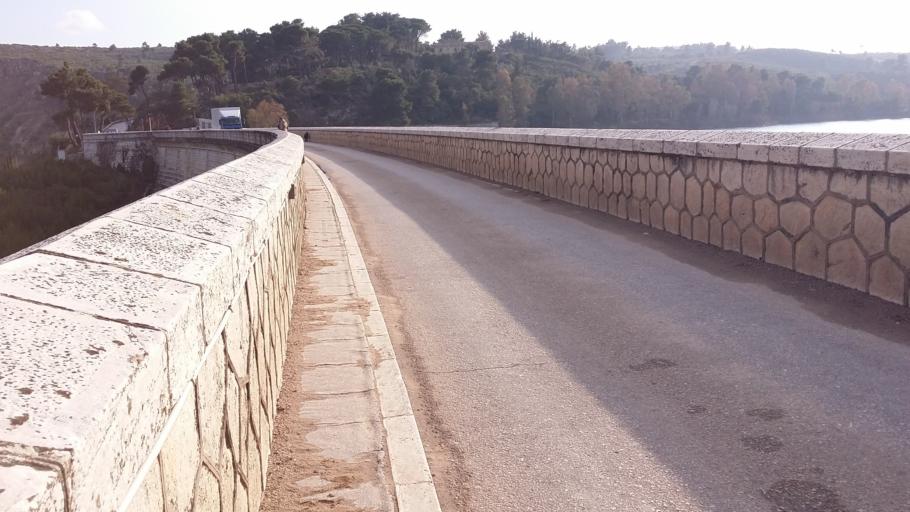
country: GR
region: Attica
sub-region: Nomarchia Anatolikis Attikis
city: Stamata
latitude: 38.1673
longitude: 23.9056
